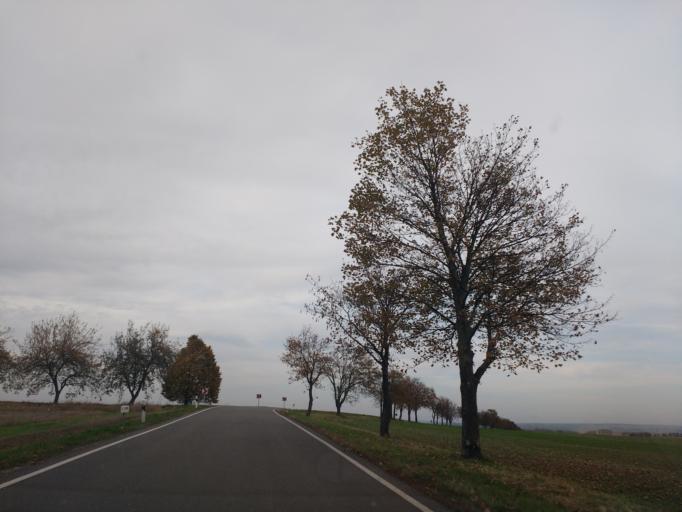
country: DE
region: Thuringia
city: Mulverstedt
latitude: 51.1234
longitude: 10.5093
